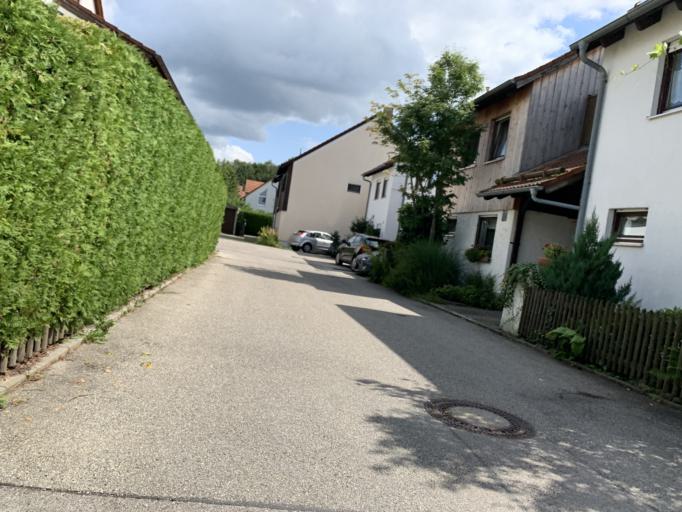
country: DE
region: Bavaria
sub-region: Upper Bavaria
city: Zolling
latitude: 48.4526
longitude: 11.7744
